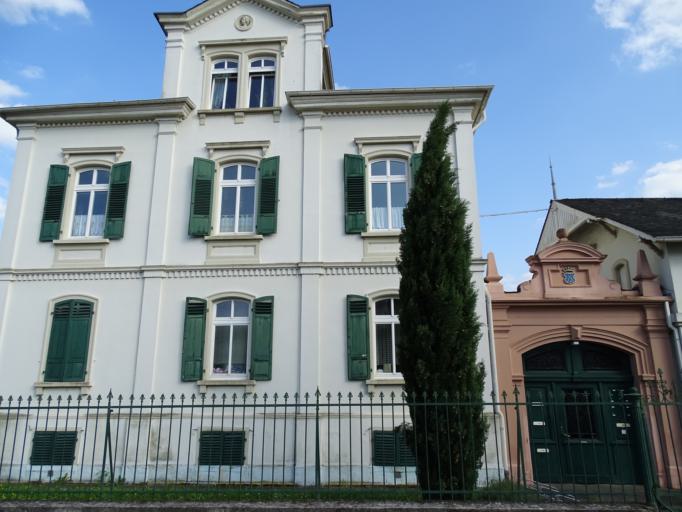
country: DE
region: Hesse
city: Geisenheim
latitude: 49.9862
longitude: 7.9716
